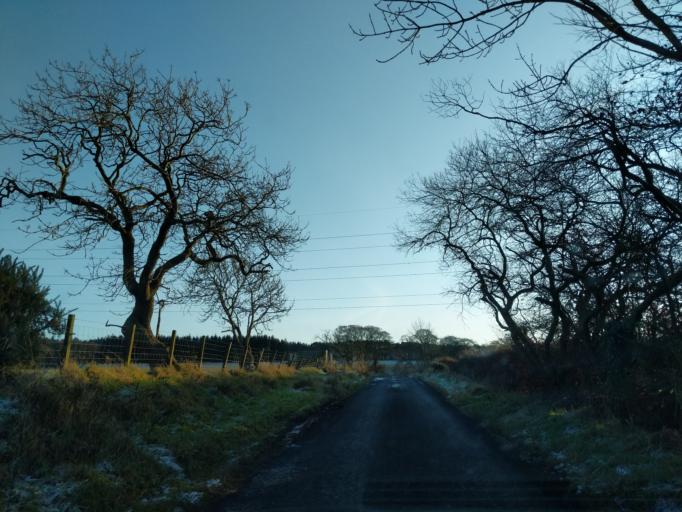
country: GB
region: Scotland
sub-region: Edinburgh
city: Balerno
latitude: 55.8662
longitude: -3.3649
